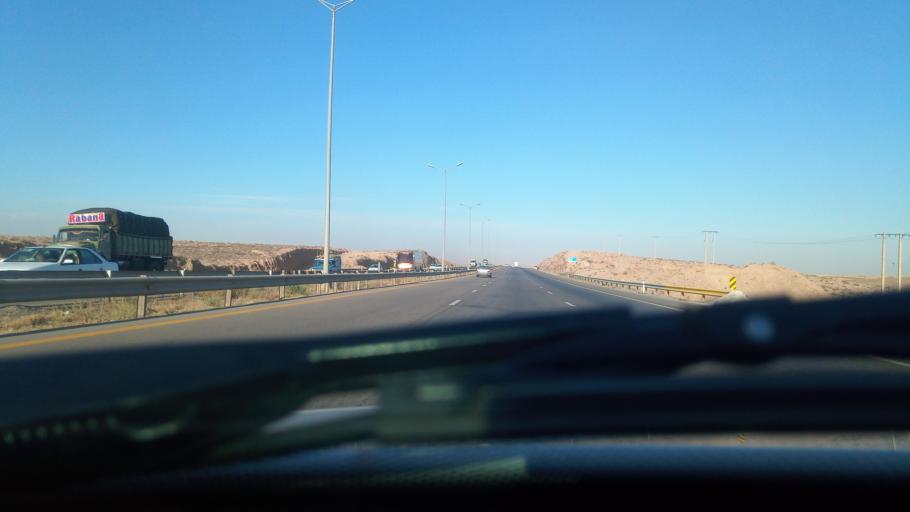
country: IR
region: Razavi Khorasan
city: Mashhad
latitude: 36.0506
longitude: 59.7087
